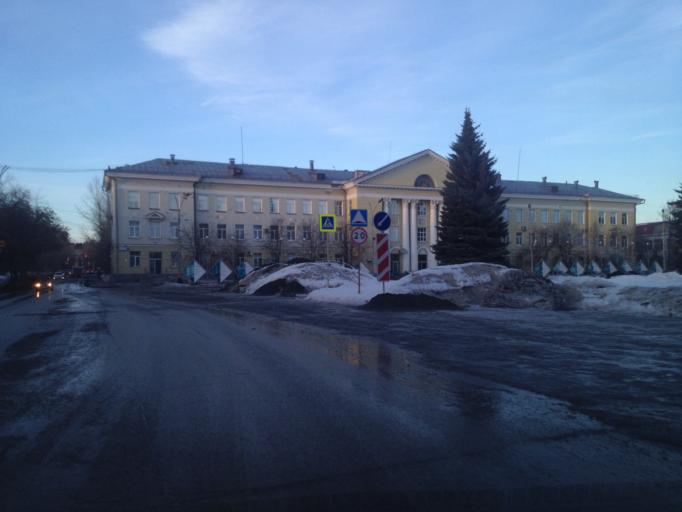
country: RU
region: Sverdlovsk
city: Istok
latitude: 56.7562
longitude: 60.7104
